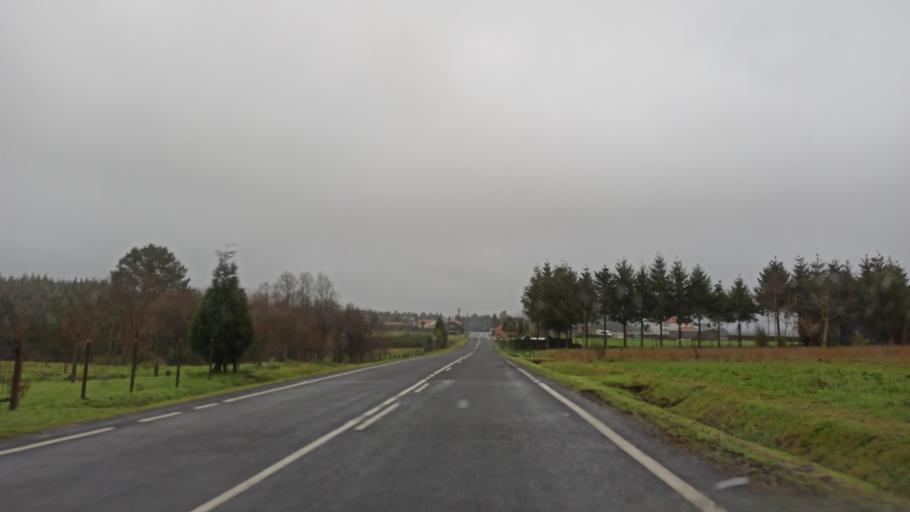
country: ES
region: Galicia
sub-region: Provincia da Coruna
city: Curtis
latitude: 43.1745
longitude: -8.1105
